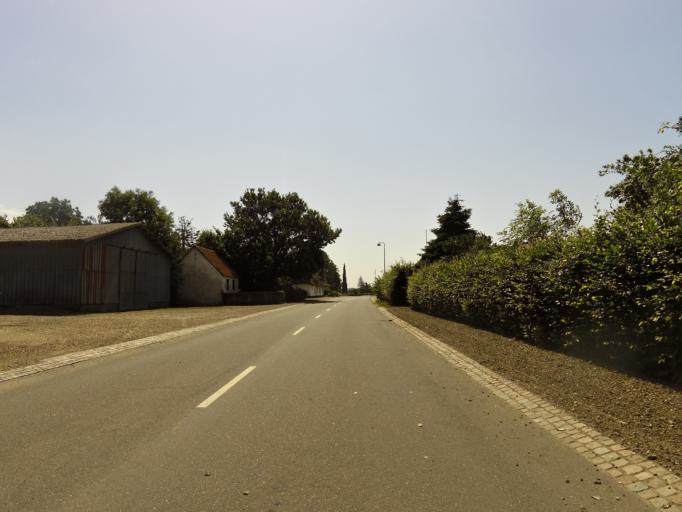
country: DK
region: South Denmark
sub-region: Haderslev Kommune
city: Vojens
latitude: 55.1595
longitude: 9.2158
